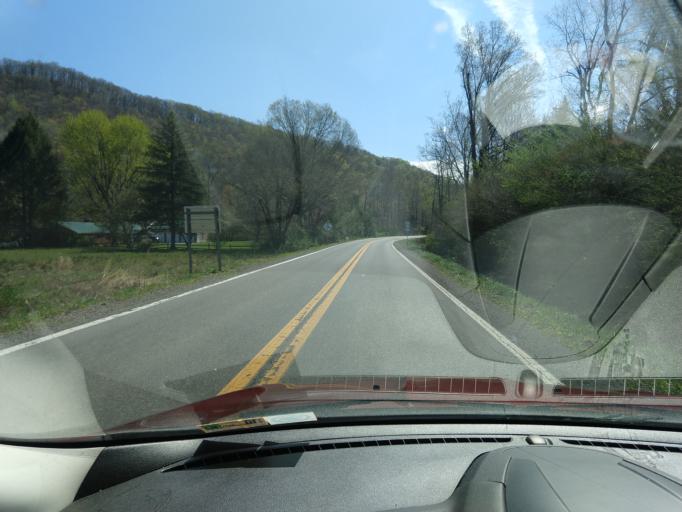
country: US
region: West Virginia
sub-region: Greenbrier County
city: Alderson
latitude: 37.7251
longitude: -80.6320
